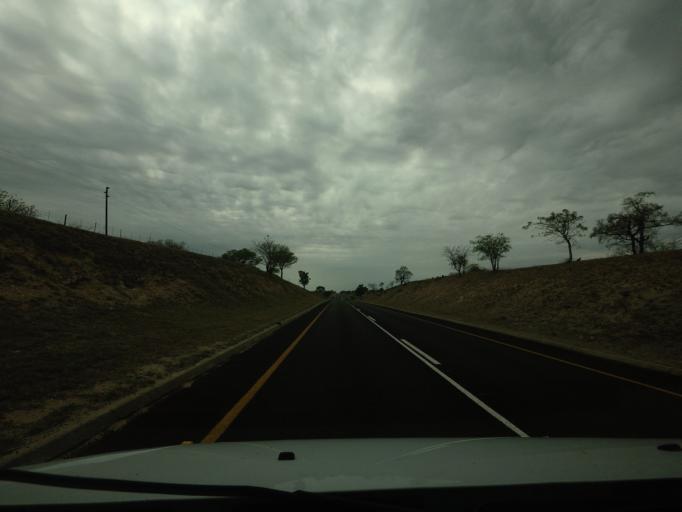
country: ZA
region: Limpopo
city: Thulamahashi
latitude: -24.5635
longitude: 31.1363
